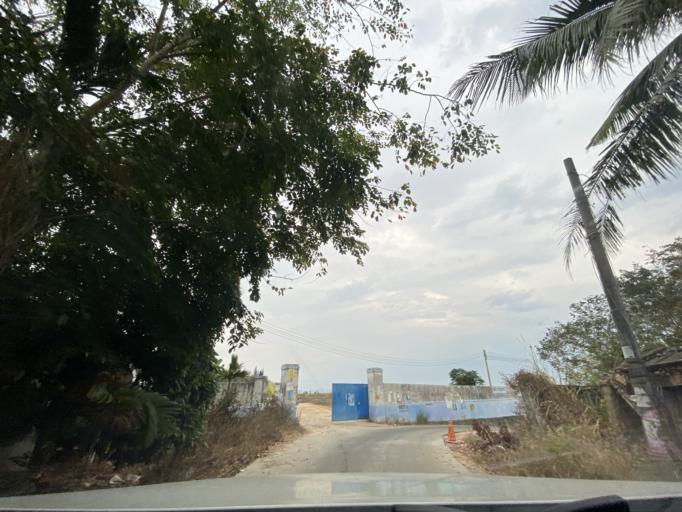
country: CN
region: Hainan
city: Yingzhou
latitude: 18.3855
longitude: 109.8192
